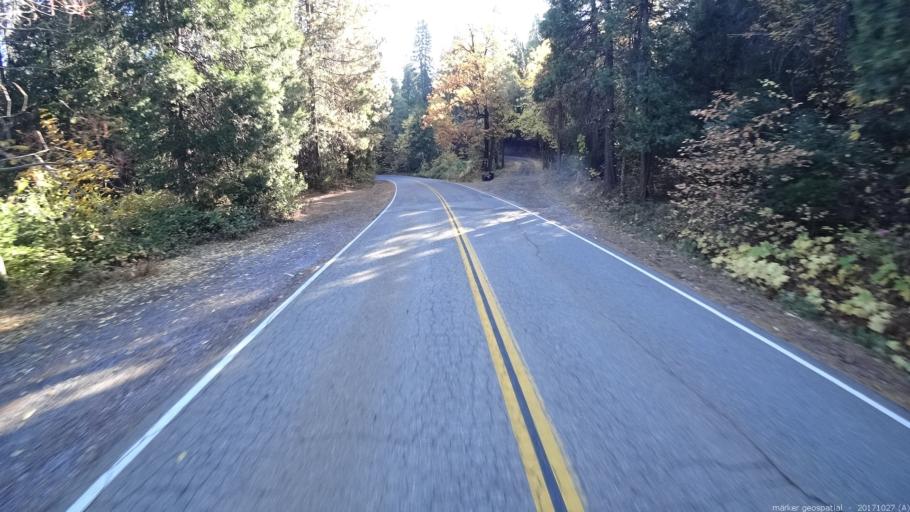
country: US
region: California
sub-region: Shasta County
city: Burney
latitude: 40.9908
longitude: -121.9215
